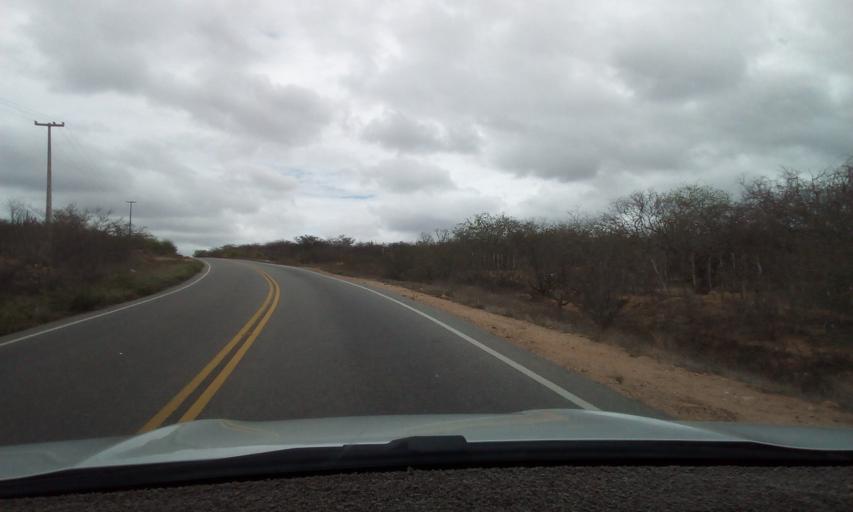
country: BR
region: Paraiba
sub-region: Picui
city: Picui
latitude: -6.5305
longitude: -36.3096
